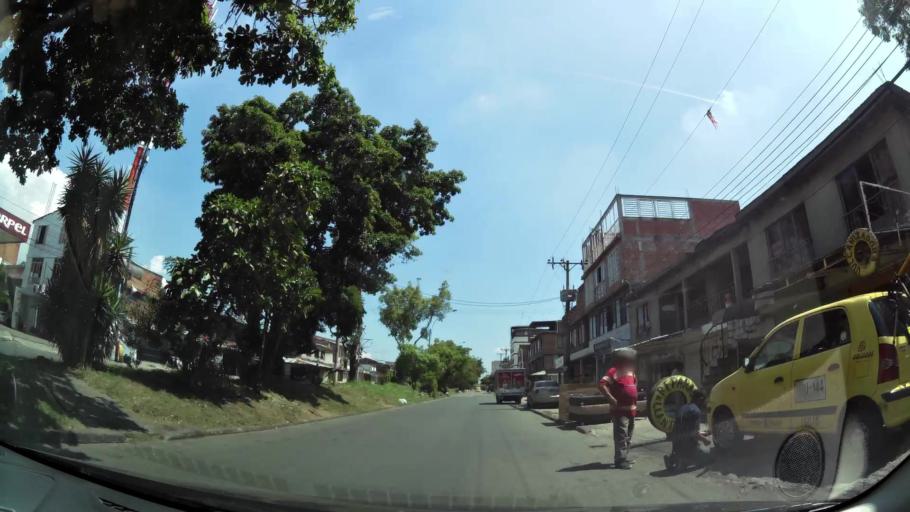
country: CO
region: Valle del Cauca
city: Cali
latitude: 3.4336
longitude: -76.5014
